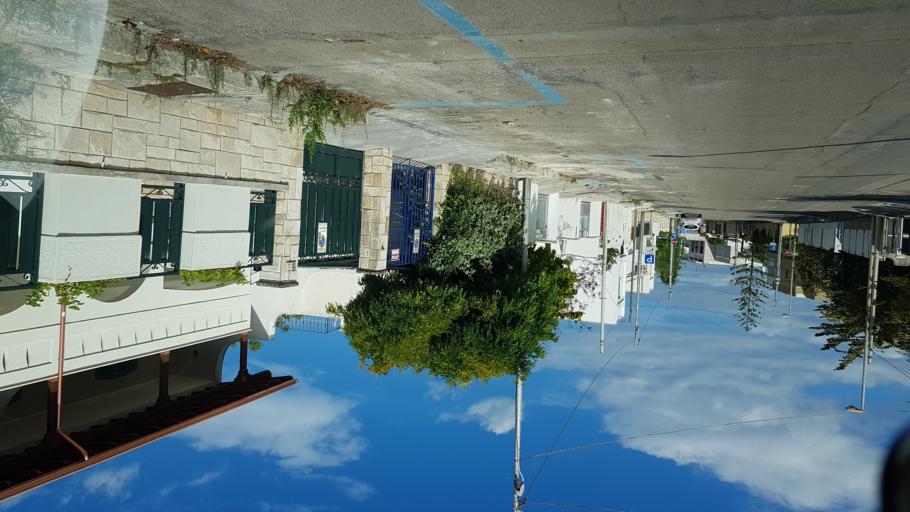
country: IT
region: Apulia
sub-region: Provincia di Lecce
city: Borgagne
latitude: 40.2713
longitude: 18.4279
